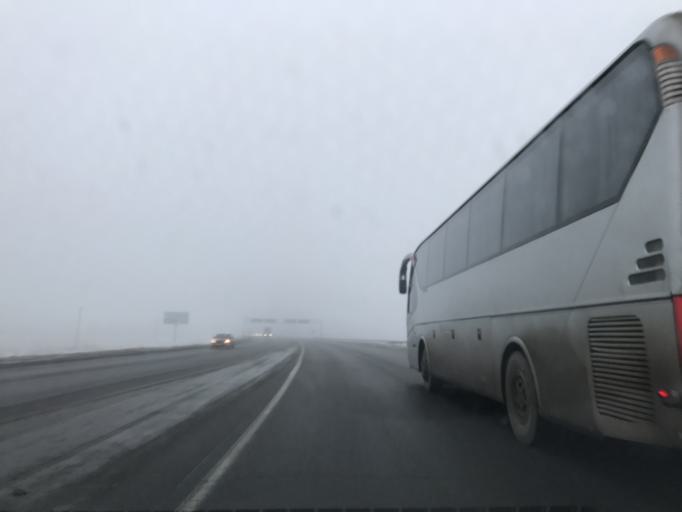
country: RU
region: Rostov
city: Grushevskaya
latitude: 47.4111
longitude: 39.9746
